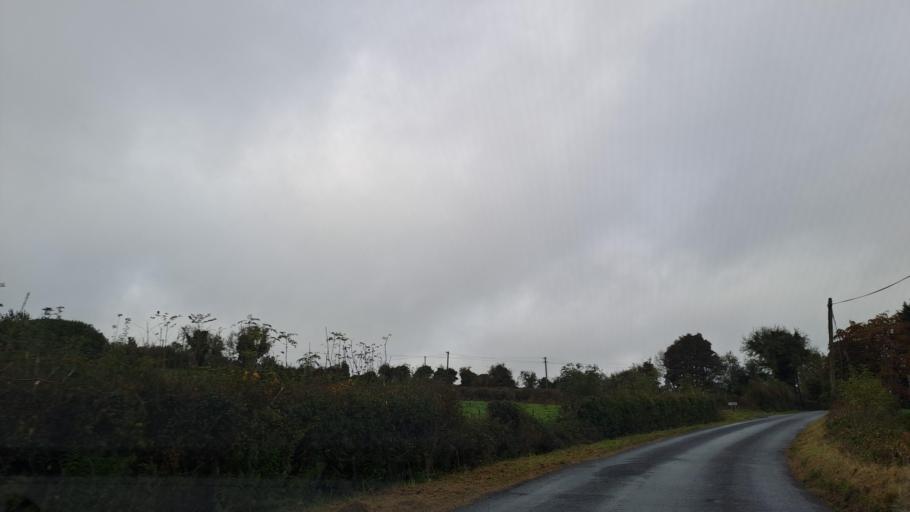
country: IE
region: Ulster
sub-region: An Cabhan
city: Bailieborough
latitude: 53.9925
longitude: -6.9435
